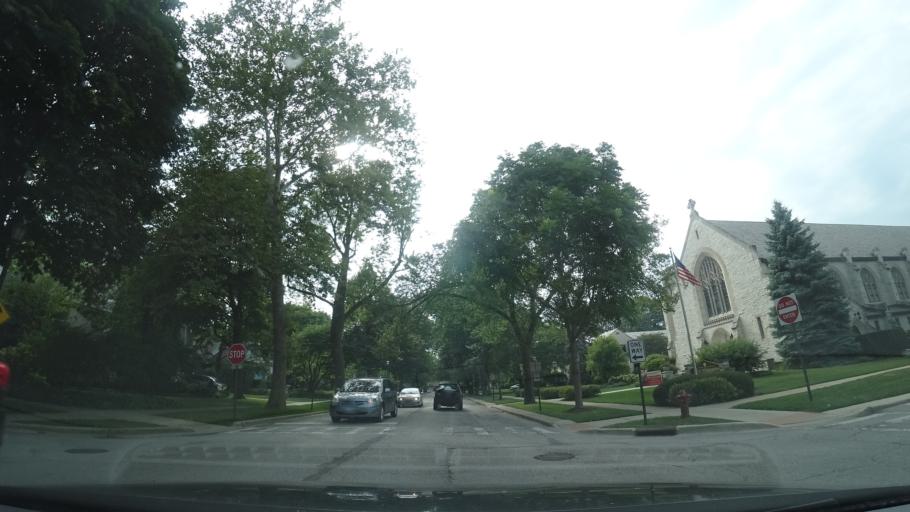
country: US
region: Illinois
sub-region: Cook County
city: Evanston
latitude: 42.0621
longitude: -87.6939
